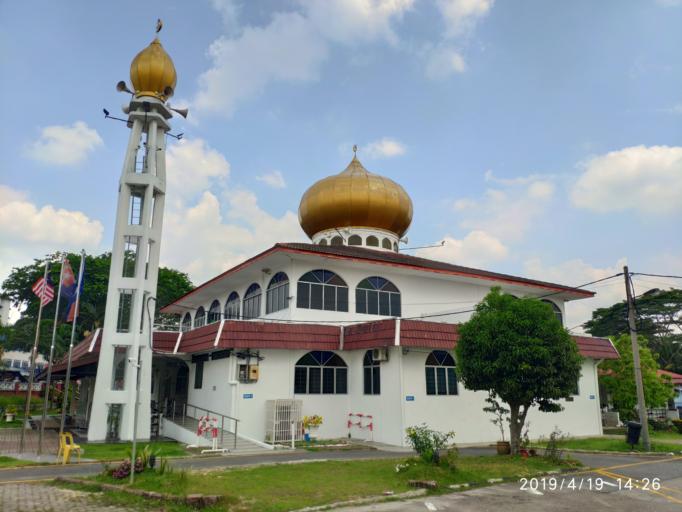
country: MY
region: Johor
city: Johor Bahru
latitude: 1.4817
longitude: 103.7722
